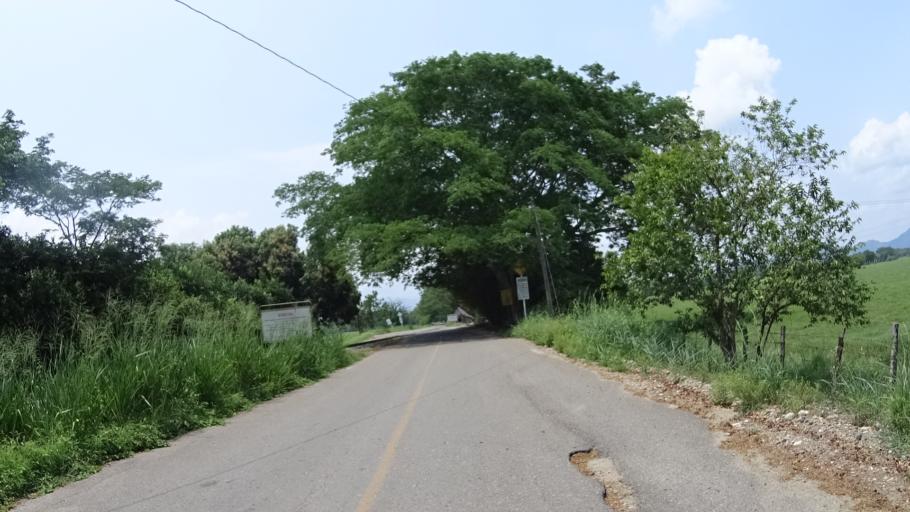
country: CO
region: Cundinamarca
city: Puerto Salgar
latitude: 5.5074
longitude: -74.6900
